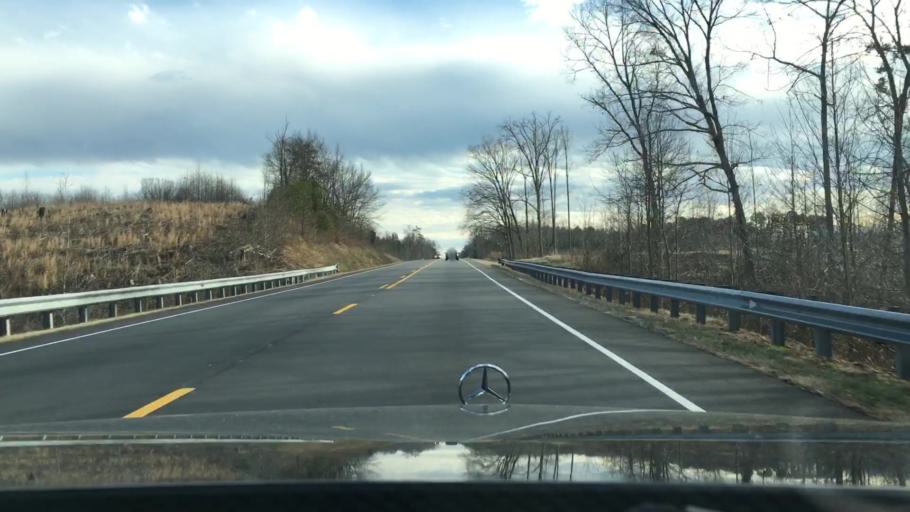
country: US
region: Virginia
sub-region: City of Danville
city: Danville
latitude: 36.5023
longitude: -79.3880
